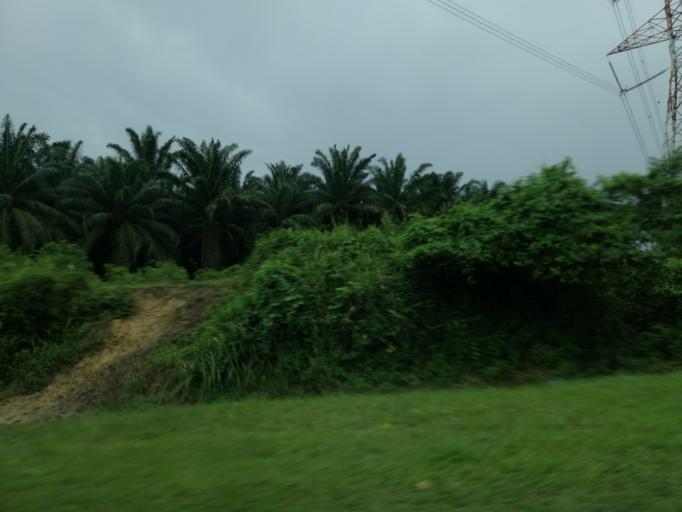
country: MY
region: Penang
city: Tasek Glugor
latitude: 5.4921
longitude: 100.6054
